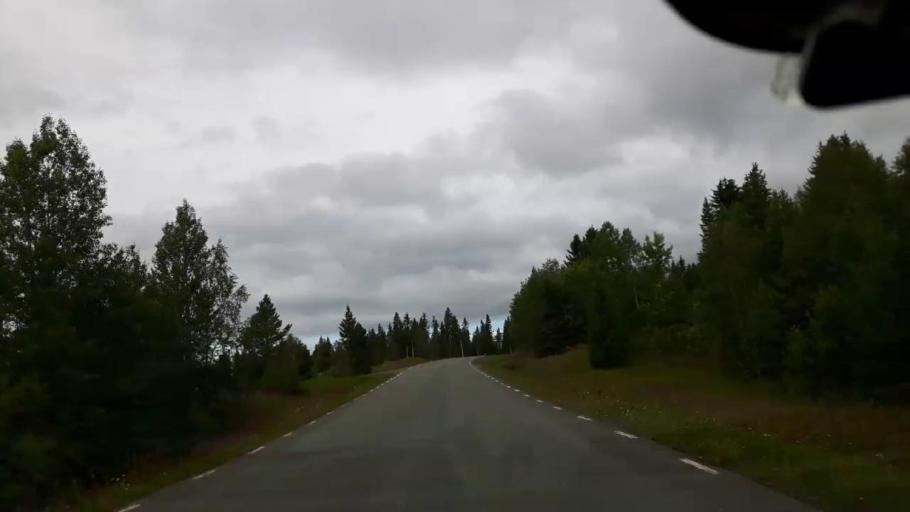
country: SE
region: Jaemtland
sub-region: Krokoms Kommun
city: Valla
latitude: 63.5126
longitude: 13.8816
